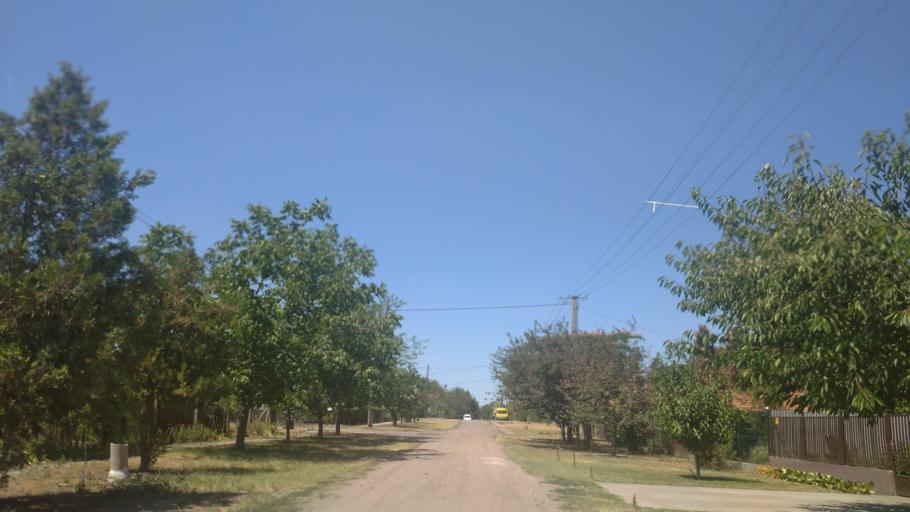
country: HU
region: Bekes
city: Oroshaza
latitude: 46.5580
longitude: 20.6203
